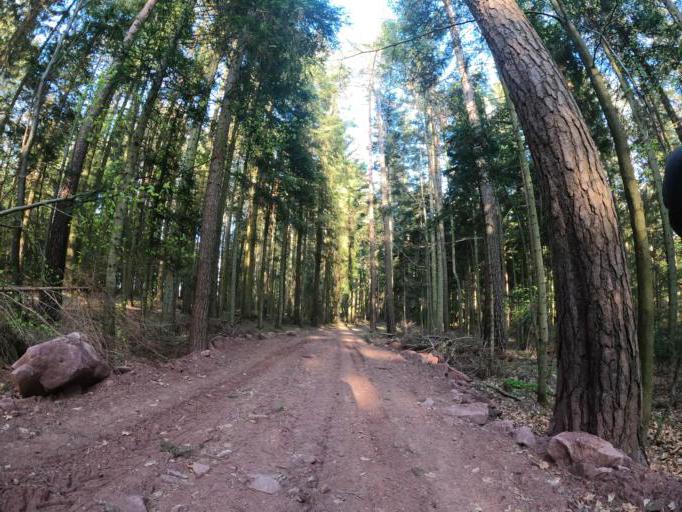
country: DE
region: Baden-Wuerttemberg
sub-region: Karlsruhe Region
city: Oberreichenbach
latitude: 48.7073
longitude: 8.6531
